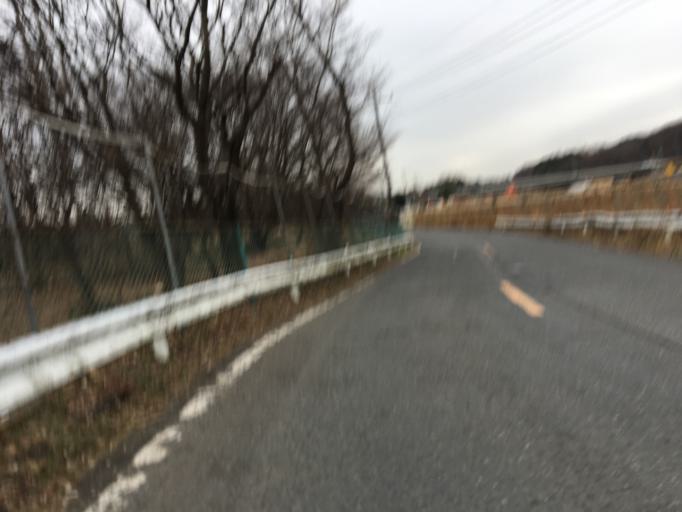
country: JP
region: Saitama
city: Oi
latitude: 35.8044
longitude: 139.5384
